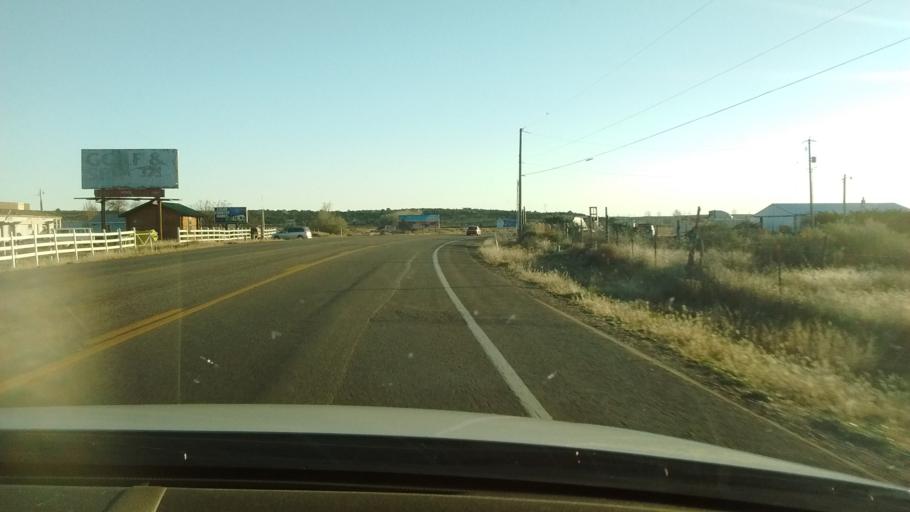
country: US
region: Utah
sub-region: Kane County
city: Kanab
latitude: 37.0146
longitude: -112.5250
